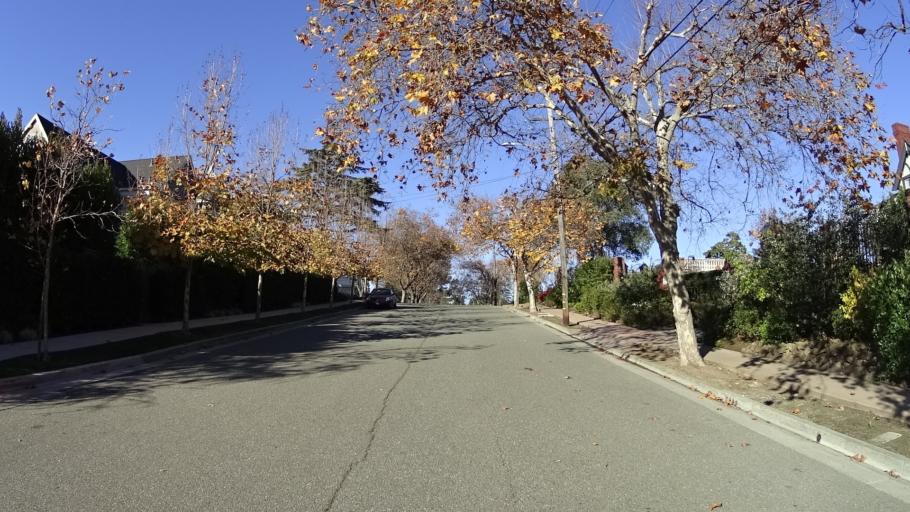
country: US
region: California
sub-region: Alameda County
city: Piedmont
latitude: 37.8160
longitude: -122.2242
